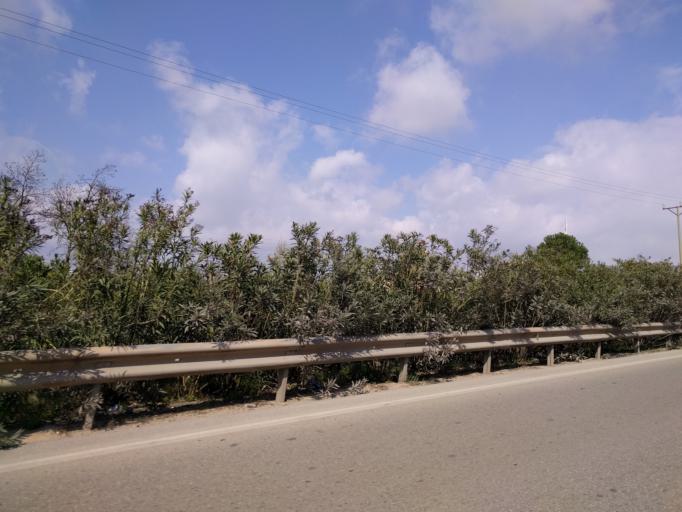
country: TR
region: Antalya
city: Antalya
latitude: 36.9001
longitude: 30.6363
